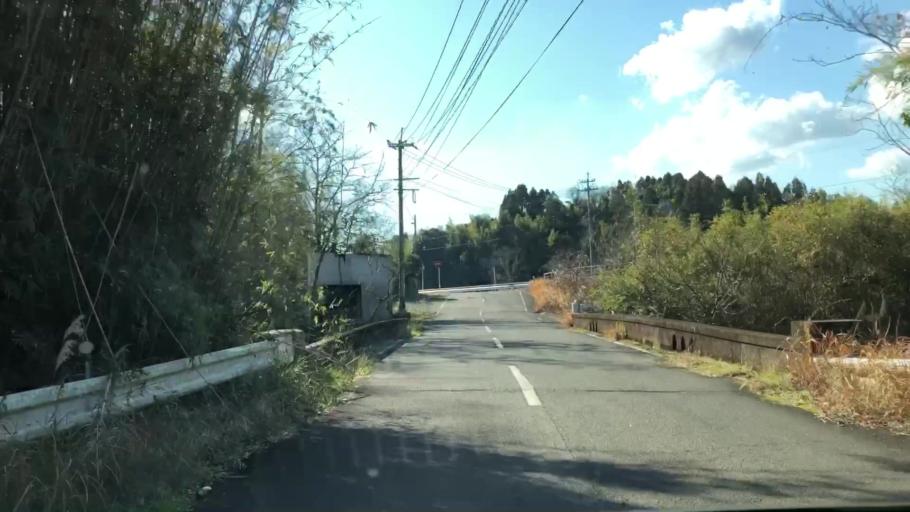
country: JP
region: Kagoshima
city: Satsumasendai
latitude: 31.8606
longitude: 130.3938
